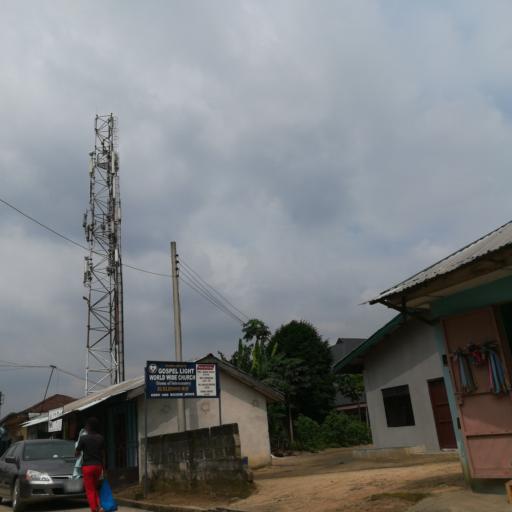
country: NG
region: Rivers
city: Port Harcourt
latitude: 4.8417
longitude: 7.0723
